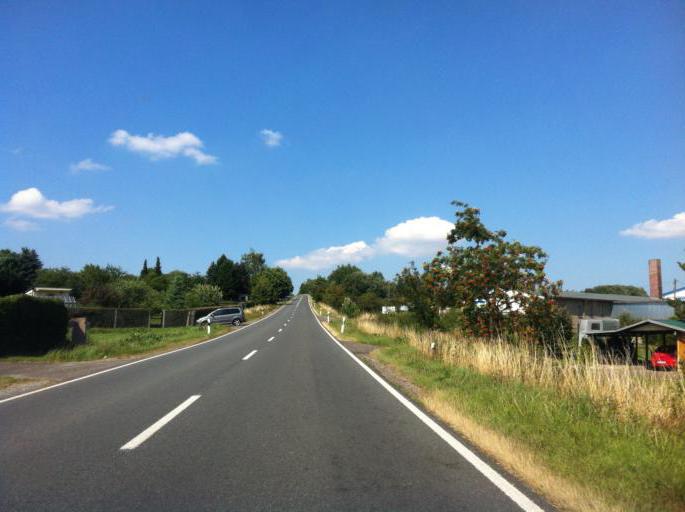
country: DE
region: Thuringia
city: Dingelstadt
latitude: 51.3200
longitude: 10.3067
